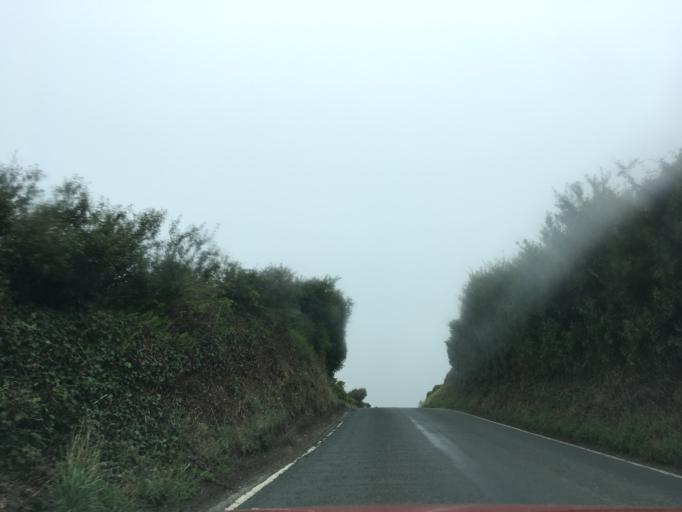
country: GB
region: Wales
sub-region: Pembrokeshire
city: Saint David's
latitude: 51.8775
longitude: -5.2104
